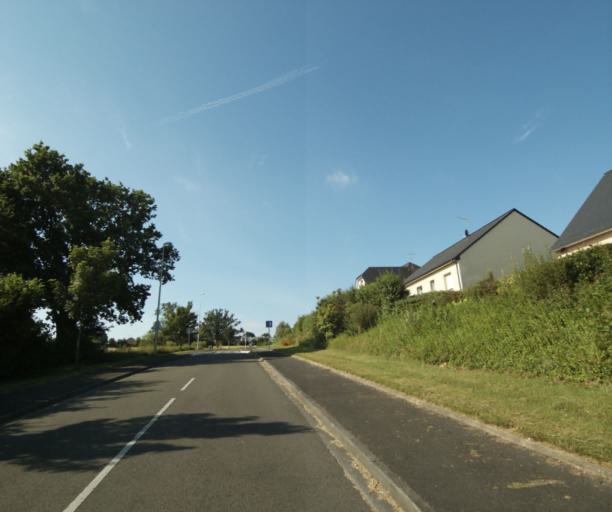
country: FR
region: Pays de la Loire
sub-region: Departement de la Mayenne
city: Laval
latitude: 48.0570
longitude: -0.7799
